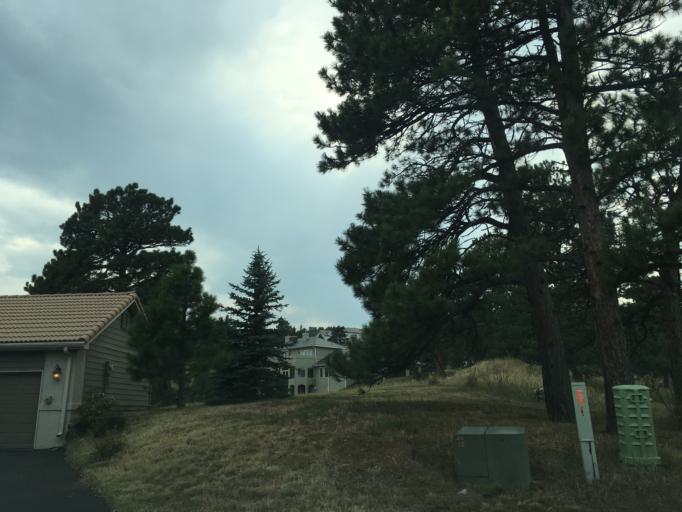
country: US
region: Colorado
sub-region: Jefferson County
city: Genesee
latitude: 39.7030
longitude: -105.2585
